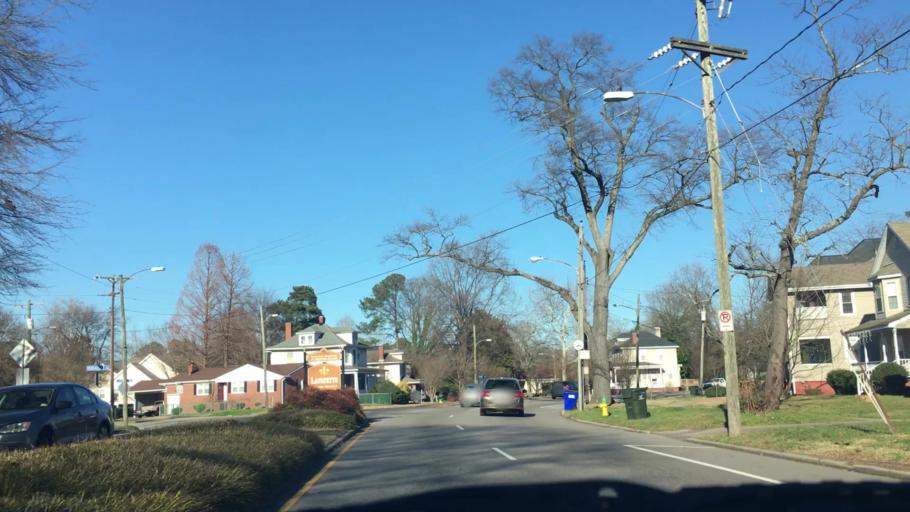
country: US
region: Virginia
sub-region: City of Norfolk
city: Norfolk
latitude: 36.8774
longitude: -76.2673
